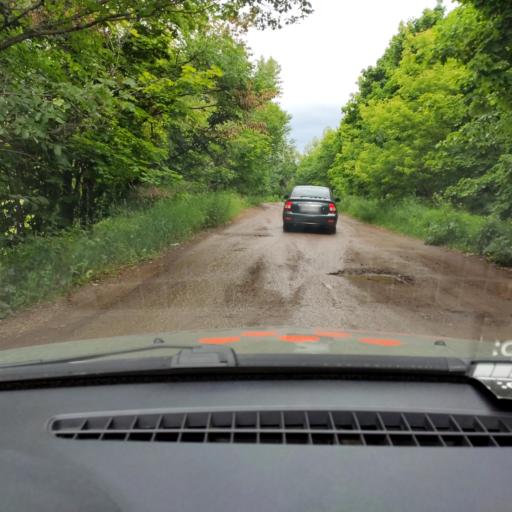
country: RU
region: Bashkortostan
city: Iglino
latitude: 54.8921
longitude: 56.2797
